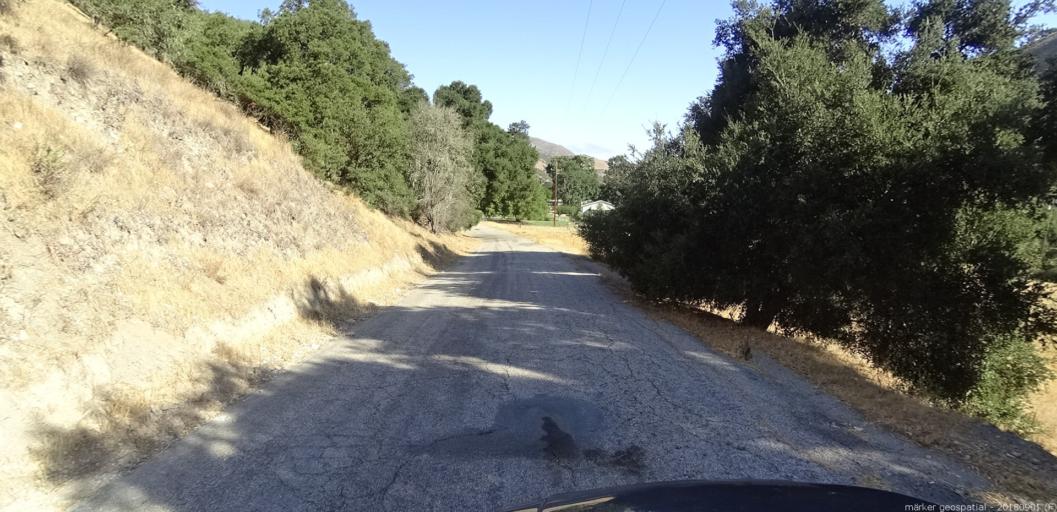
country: US
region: California
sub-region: Monterey County
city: Greenfield
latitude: 36.2033
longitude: -121.2767
